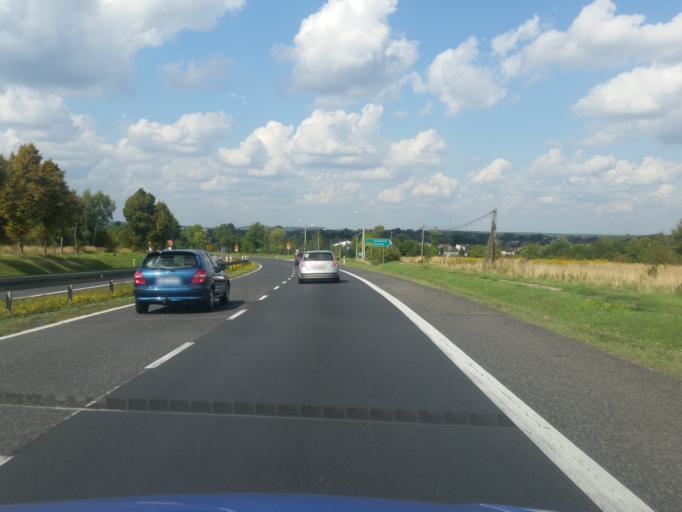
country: PL
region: Silesian Voivodeship
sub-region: Powiat myszkowski
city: Kozieglowy
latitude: 50.5872
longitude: 19.1626
